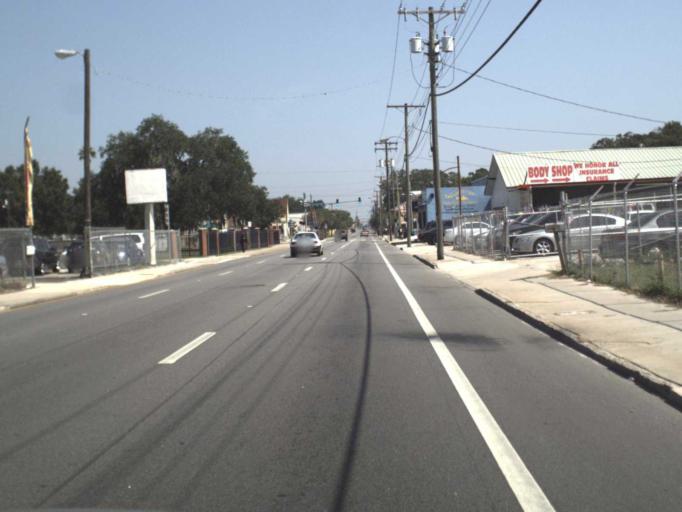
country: US
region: Florida
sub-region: Hillsborough County
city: Tampa
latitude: 27.9696
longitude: -82.4594
